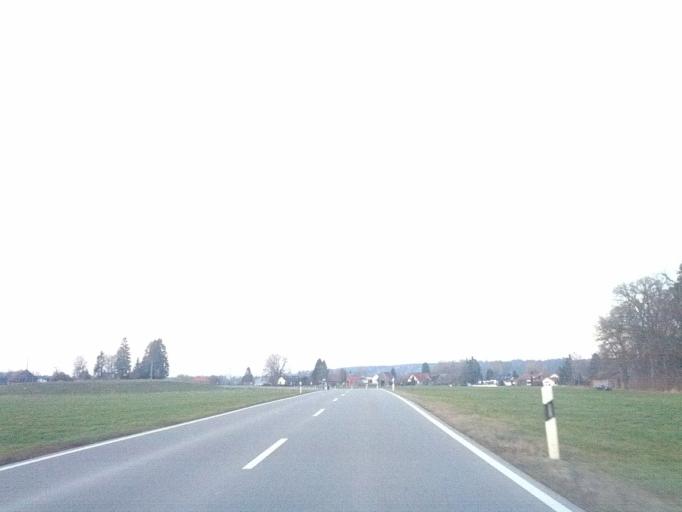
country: DE
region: Bavaria
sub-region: Swabia
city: Lautrach
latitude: 47.9121
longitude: 10.1143
